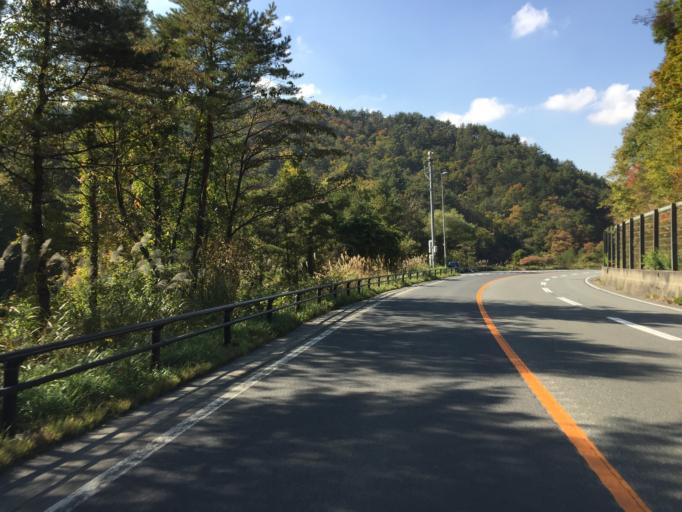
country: JP
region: Yamagata
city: Yonezawa
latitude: 37.8759
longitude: 140.2007
